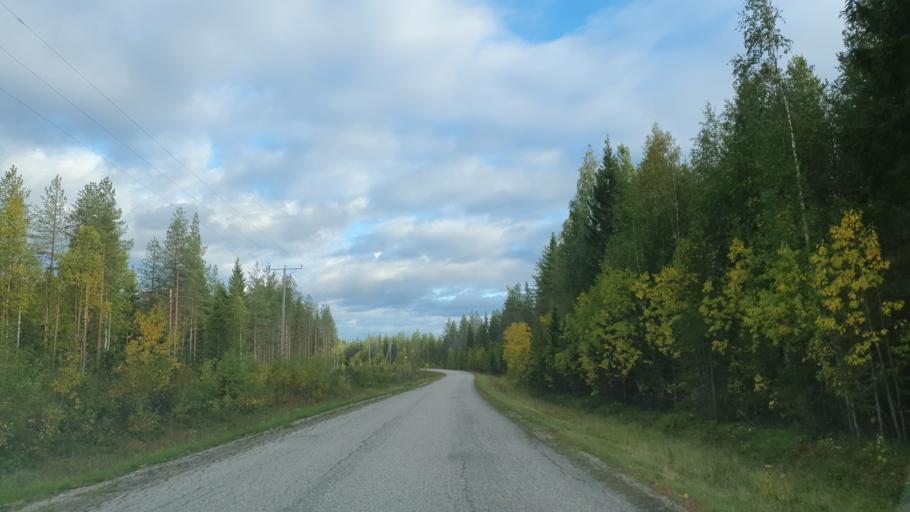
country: FI
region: Kainuu
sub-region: Kehys-Kainuu
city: Kuhmo
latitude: 63.9201
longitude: 30.0562
